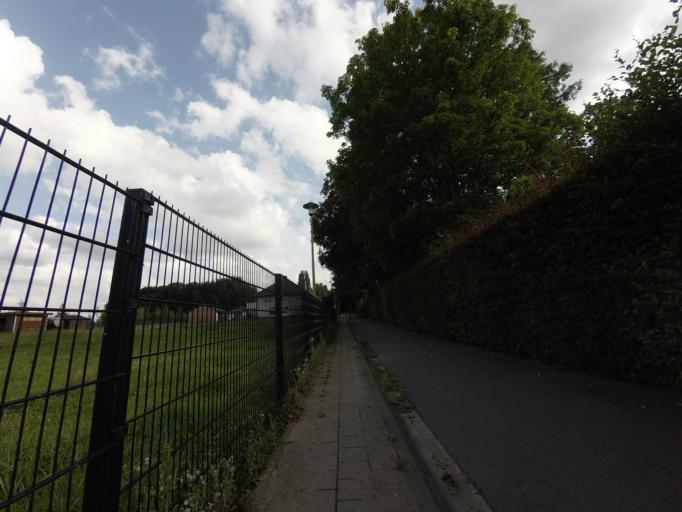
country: BE
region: Flanders
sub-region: Provincie Vlaams-Brabant
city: Grimbergen
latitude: 50.9510
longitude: 4.3692
